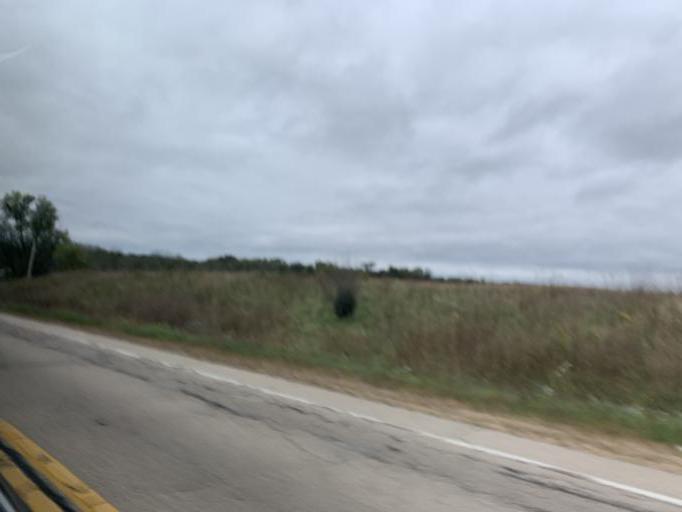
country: US
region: Wisconsin
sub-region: Grant County
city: Muscoda
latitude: 43.2198
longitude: -90.5557
